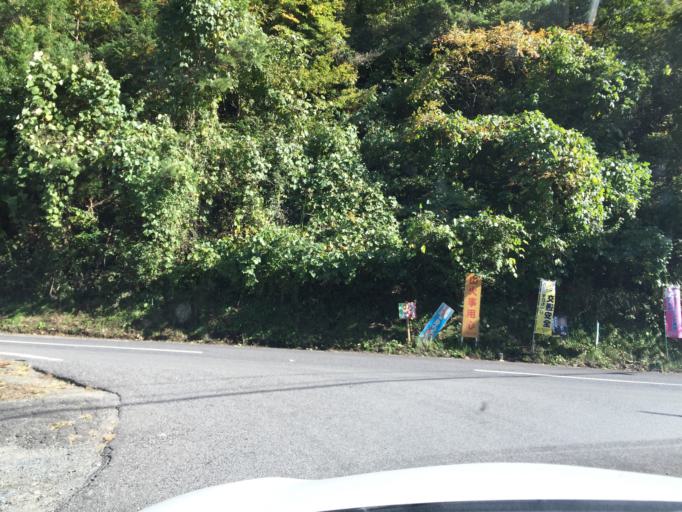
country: JP
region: Fukushima
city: Ishikawa
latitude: 37.2042
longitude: 140.5866
